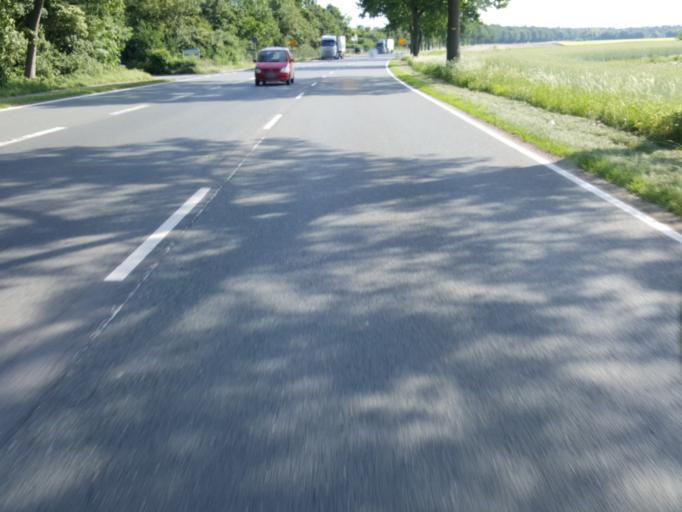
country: DE
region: Lower Saxony
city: Estorf
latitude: 52.6005
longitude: 9.1575
